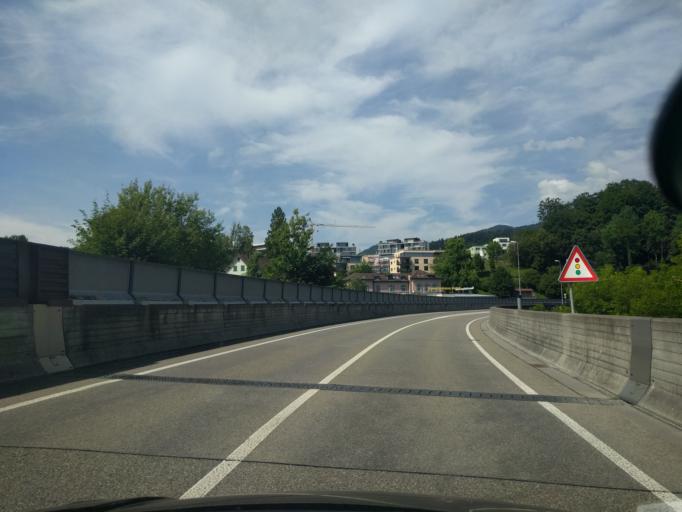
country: CH
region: Saint Gallen
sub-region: Wahlkreis See-Gaster
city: Schmerikon
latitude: 47.2419
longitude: 8.9481
